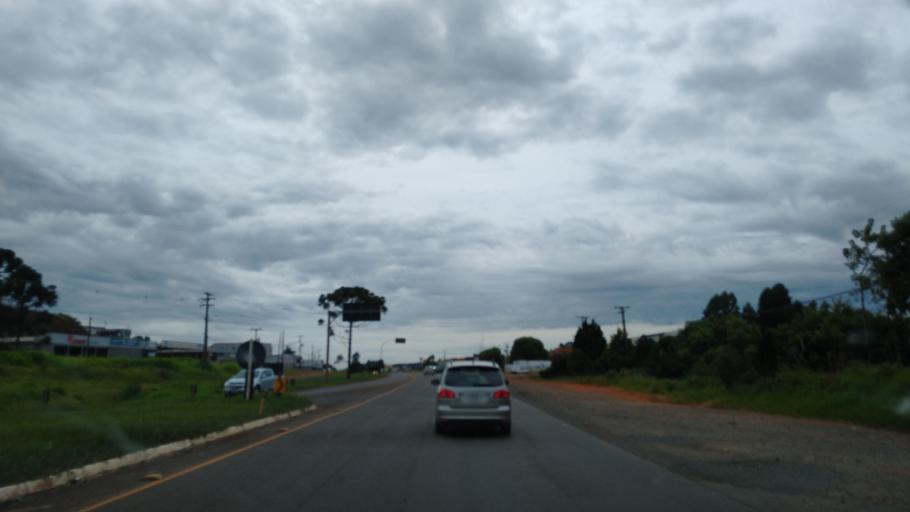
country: BR
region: Parana
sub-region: Pato Branco
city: Pato Branco
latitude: -26.2706
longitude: -52.7108
